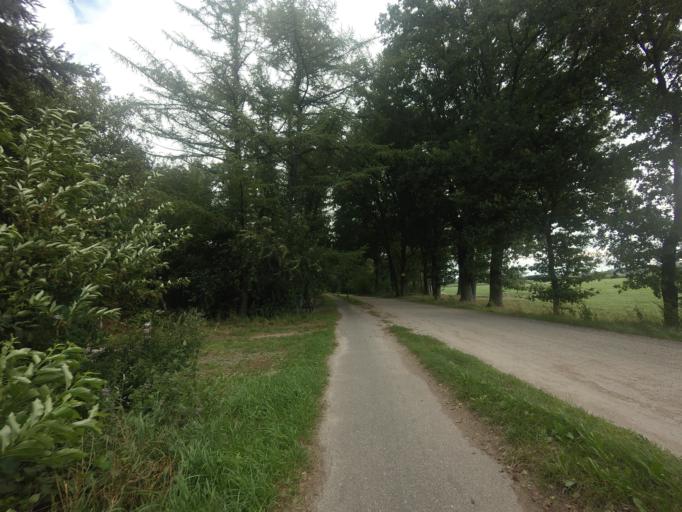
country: NL
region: Overijssel
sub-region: Gemeente Twenterand
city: Den Ham
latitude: 52.4866
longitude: 6.3798
